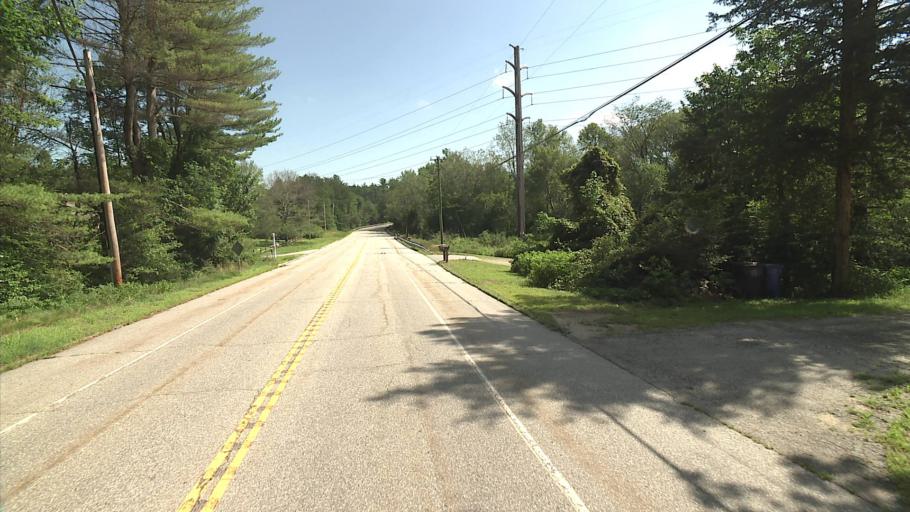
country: US
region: Connecticut
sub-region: Windham County
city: Plainfield Village
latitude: 41.7085
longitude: -71.9395
